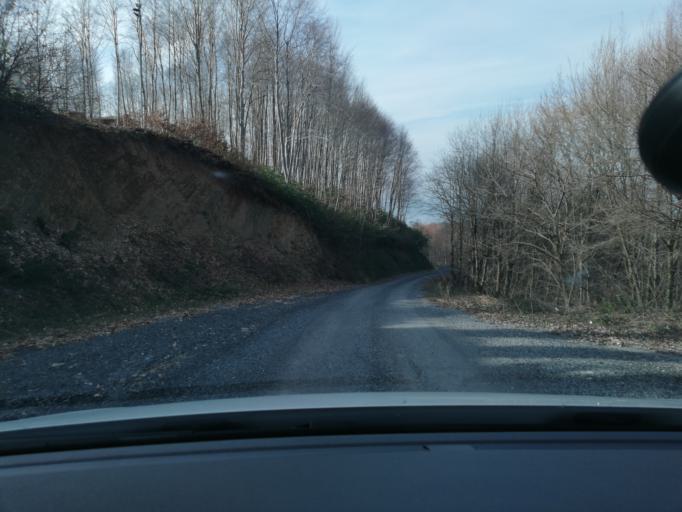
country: TR
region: Zonguldak
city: Kozlu
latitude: 41.3490
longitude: 31.6348
